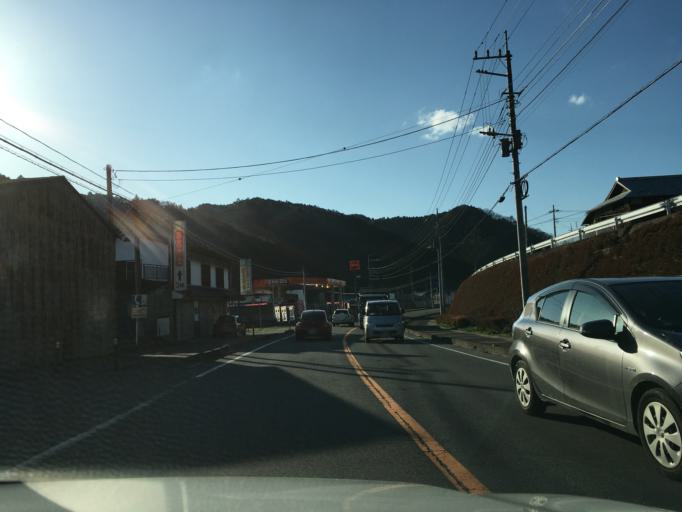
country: JP
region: Ibaraki
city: Daigo
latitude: 36.7612
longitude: 140.3610
